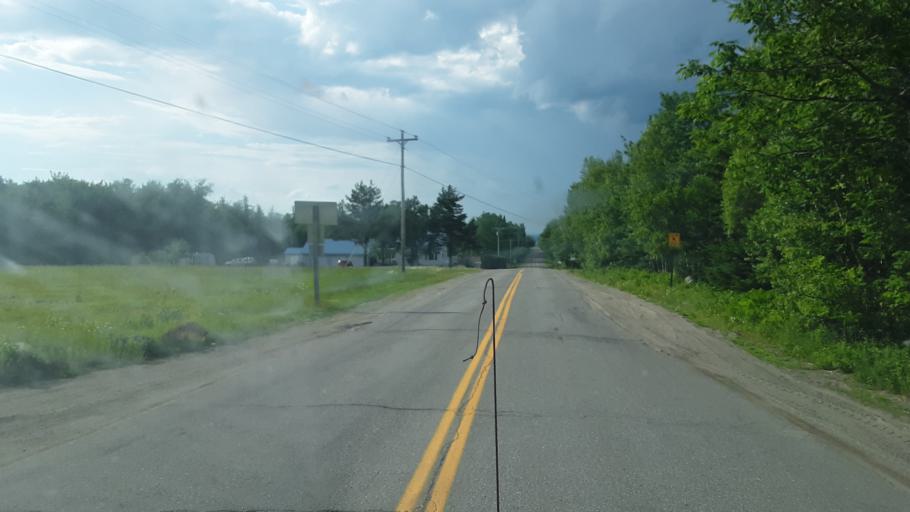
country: US
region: Maine
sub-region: Washington County
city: Calais
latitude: 45.0866
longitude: -67.5026
